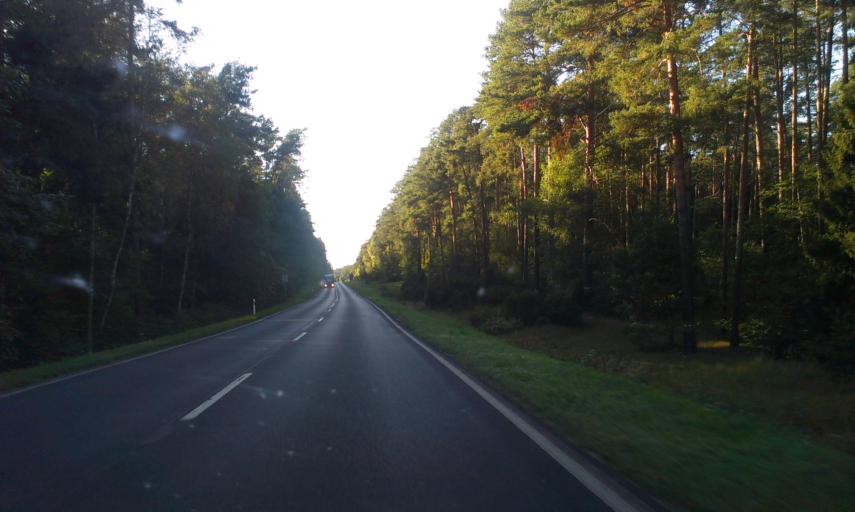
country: PL
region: Kujawsko-Pomorskie
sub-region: Powiat tucholski
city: Tuchola
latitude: 53.5526
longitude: 17.9176
